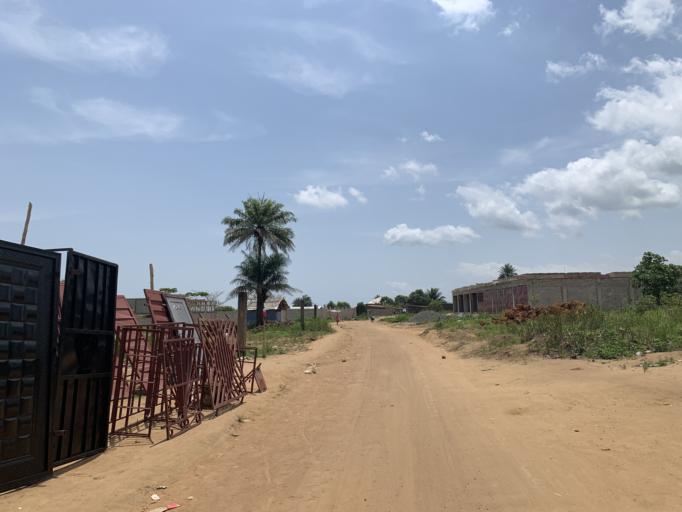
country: SL
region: Western Area
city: Waterloo
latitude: 8.3377
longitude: -13.0252
